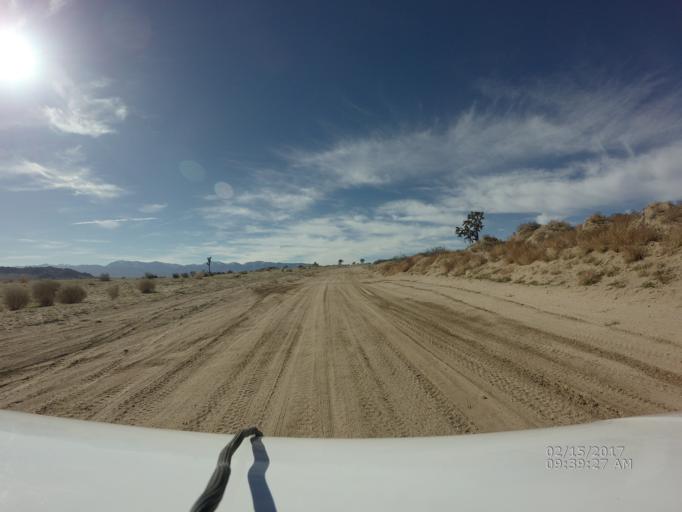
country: US
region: California
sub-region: Los Angeles County
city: Lake Los Angeles
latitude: 34.6299
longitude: -117.8855
